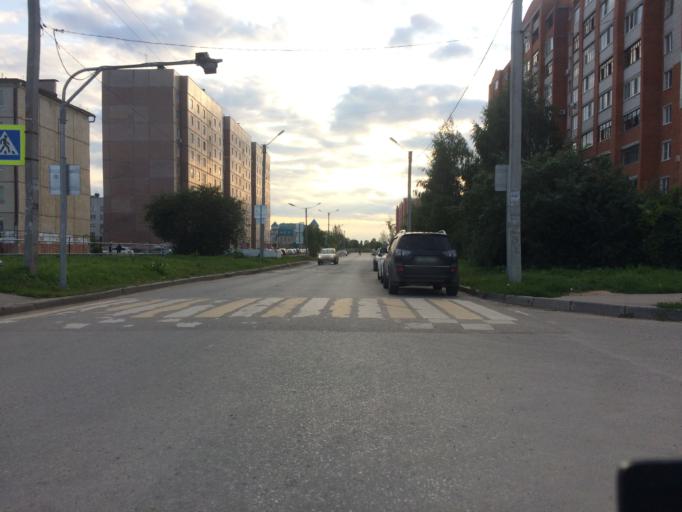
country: RU
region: Mariy-El
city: Medvedevo
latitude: 56.6447
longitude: 47.8390
